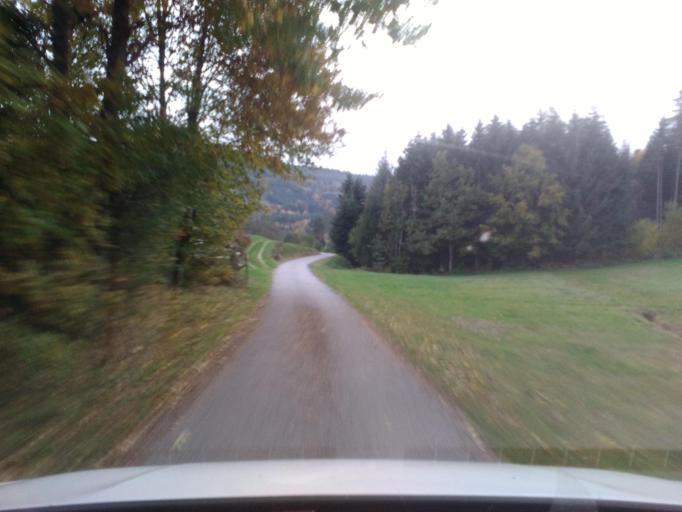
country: FR
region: Lorraine
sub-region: Departement des Vosges
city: Le Tholy
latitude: 48.0765
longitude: 6.7377
